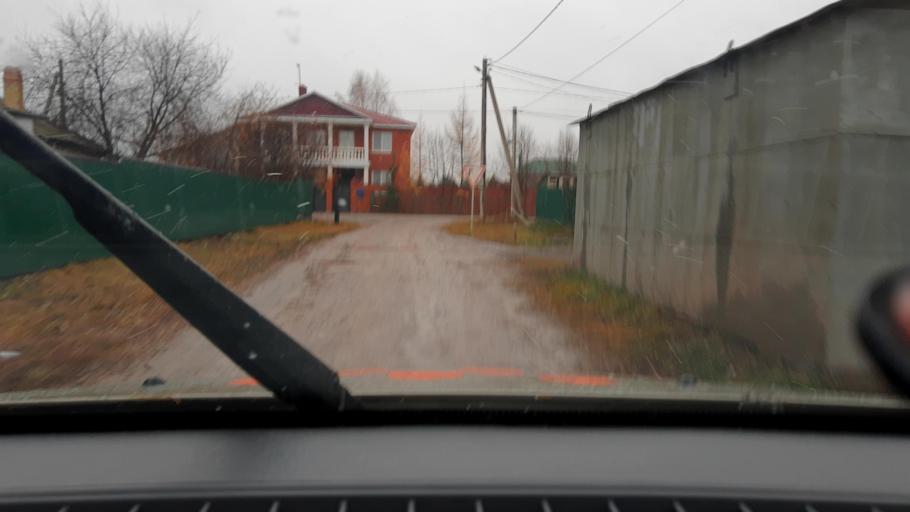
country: RU
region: Bashkortostan
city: Ufa
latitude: 54.6139
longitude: 55.9403
